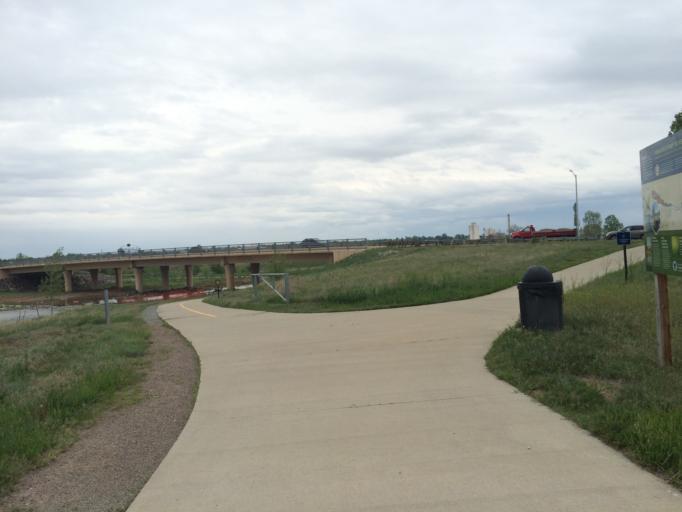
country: US
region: Colorado
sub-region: Boulder County
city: Longmont
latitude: 40.1541
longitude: -105.0938
